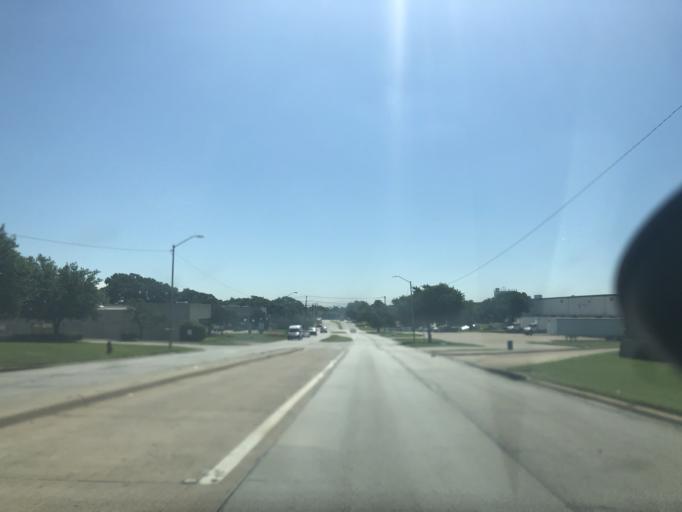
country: US
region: Texas
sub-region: Dallas County
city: Grand Prairie
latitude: 32.7853
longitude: -97.0405
